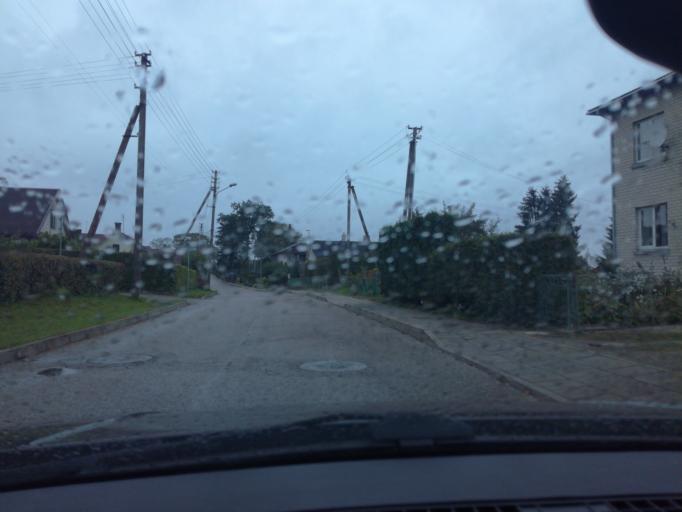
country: LT
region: Alytaus apskritis
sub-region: Alytus
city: Alytus
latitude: 54.3966
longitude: 24.0614
